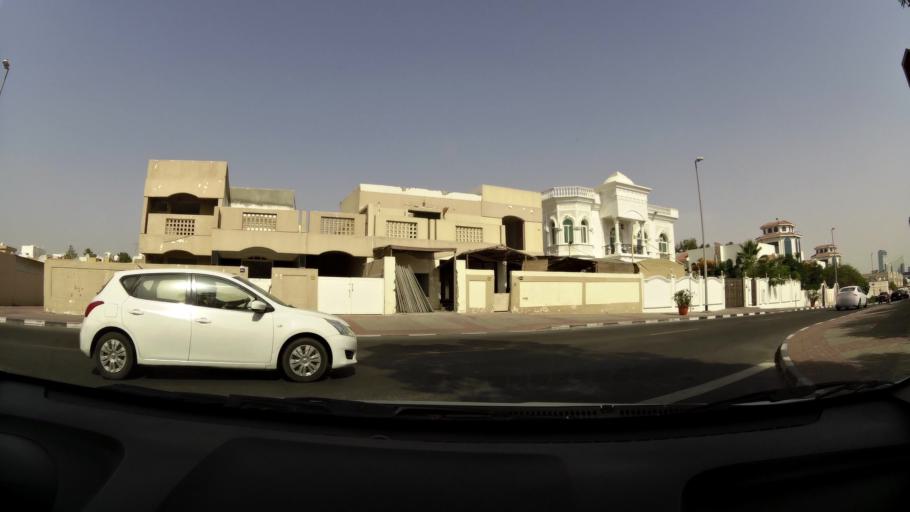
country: AE
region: Ash Shariqah
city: Sharjah
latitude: 25.2416
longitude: 55.3475
